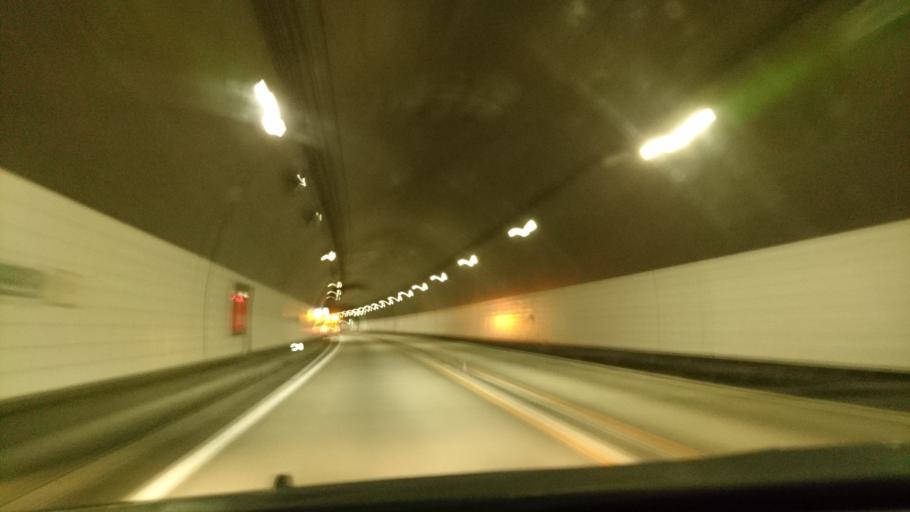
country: JP
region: Iwate
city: Tono
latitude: 39.2442
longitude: 141.6378
